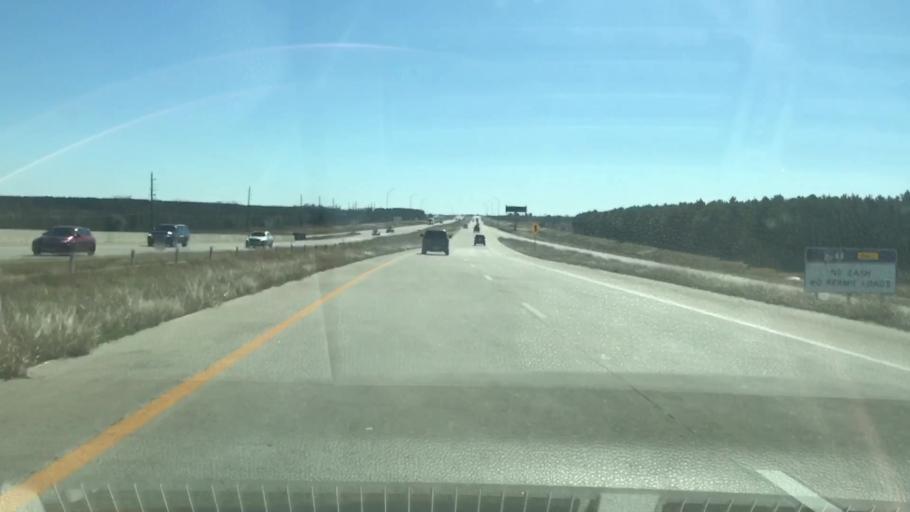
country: US
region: Texas
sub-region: Harris County
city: Cypress
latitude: 29.9026
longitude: -95.7584
